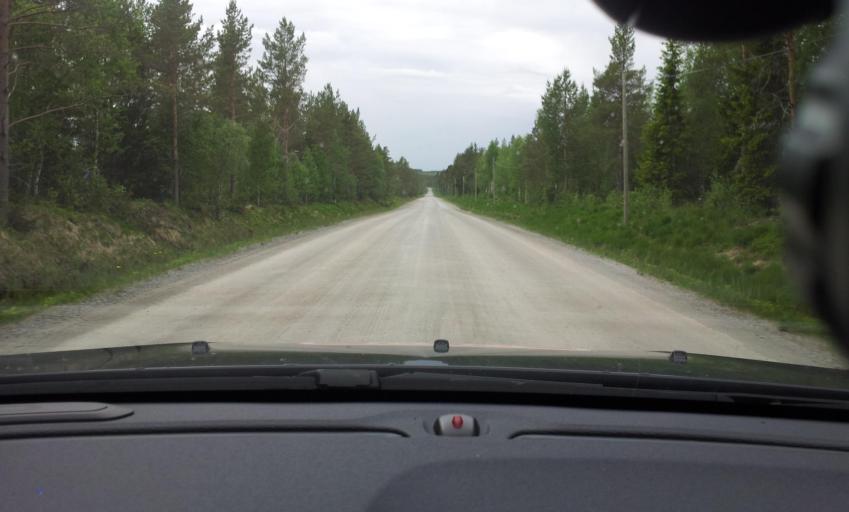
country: SE
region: Jaemtland
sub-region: OEstersunds Kommun
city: Brunflo
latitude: 63.0978
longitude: 14.9323
